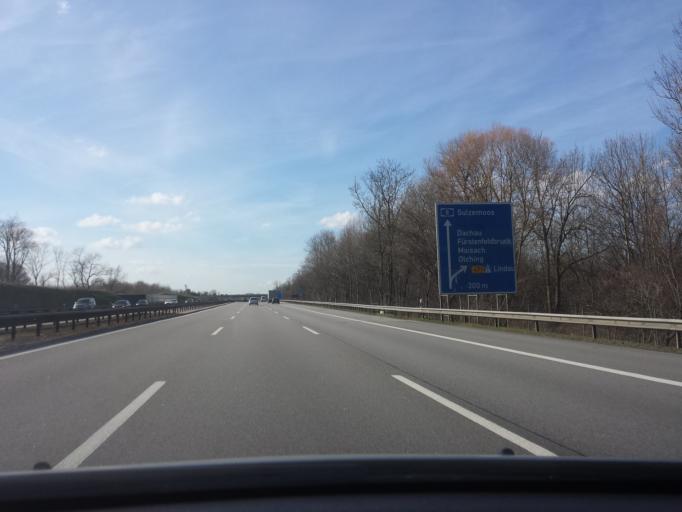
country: DE
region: Bavaria
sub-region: Upper Bavaria
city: Bergkirchen
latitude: 48.2292
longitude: 11.3558
